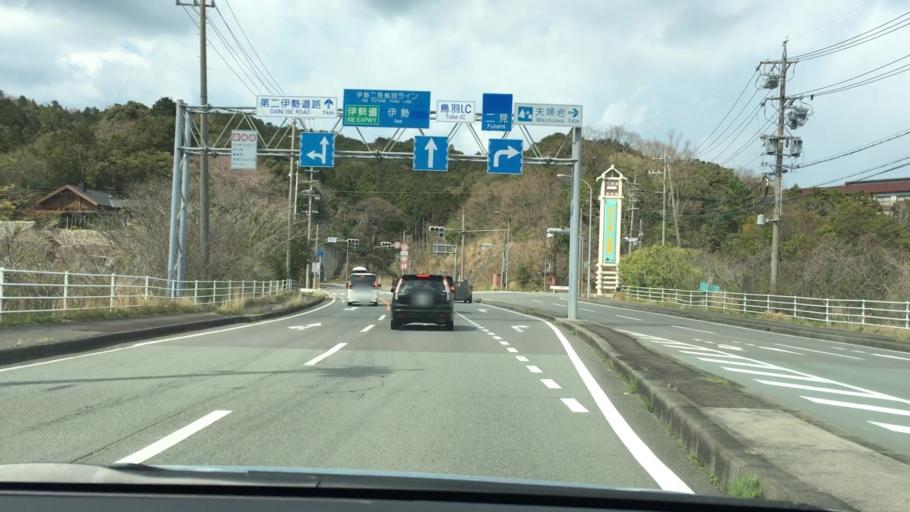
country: JP
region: Mie
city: Toba
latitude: 34.4853
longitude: 136.8159
